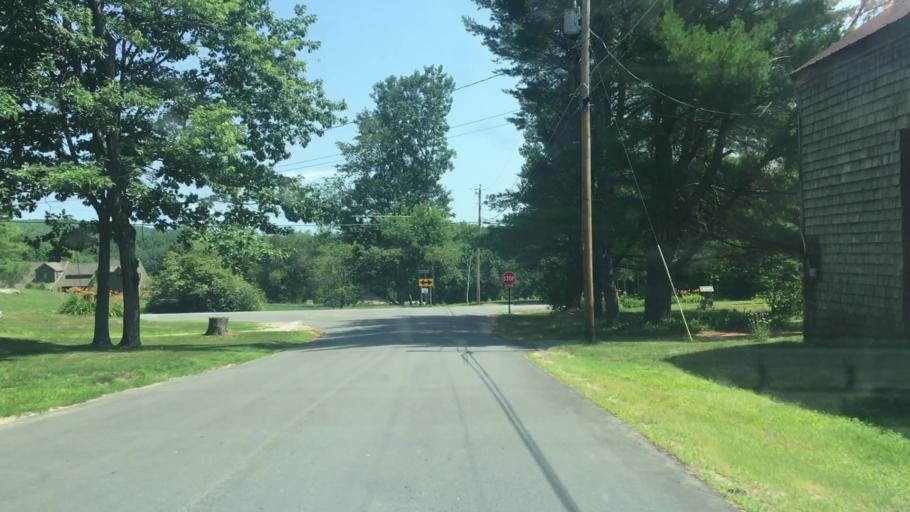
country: US
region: Maine
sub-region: Kennebec County
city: Monmouth
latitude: 44.2739
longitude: -70.0489
